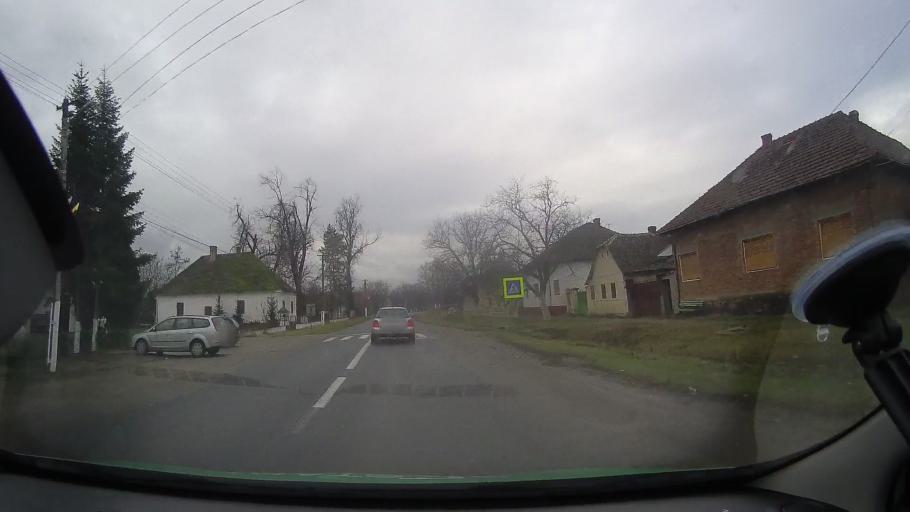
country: RO
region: Arad
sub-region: Comuna Buteni
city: Buteni
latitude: 46.3302
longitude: 22.1247
